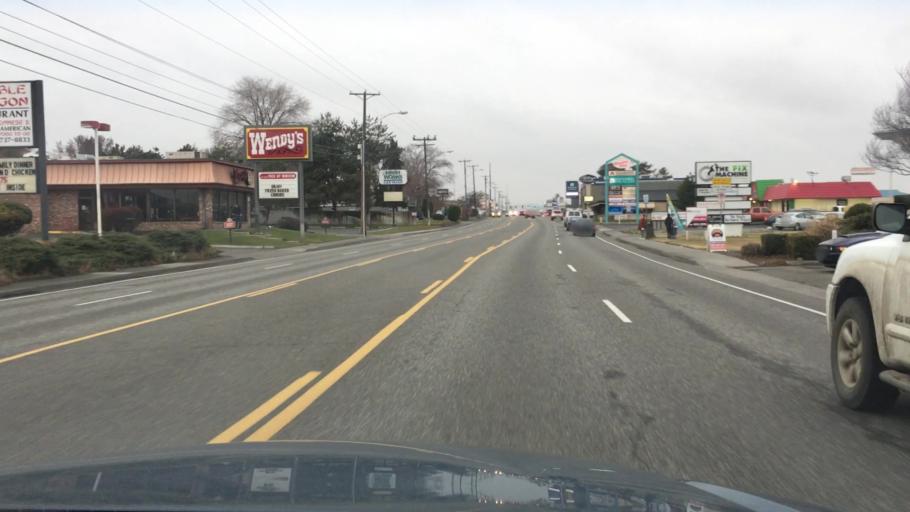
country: US
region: Washington
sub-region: Benton County
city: Kennewick
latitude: 46.2123
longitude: -119.1626
